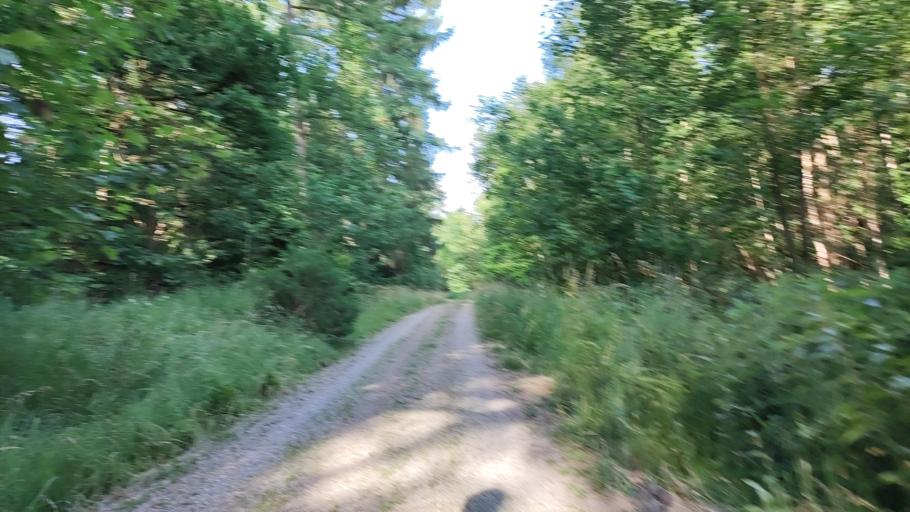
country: DE
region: Bavaria
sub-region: Swabia
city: Landensberg
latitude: 48.4174
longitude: 10.5005
